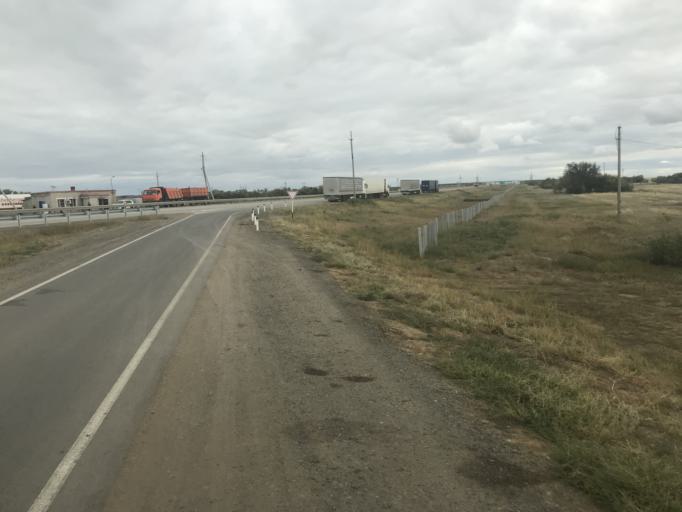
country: KZ
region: Pavlodar
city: Qalqaman
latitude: 51.9491
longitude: 75.9836
